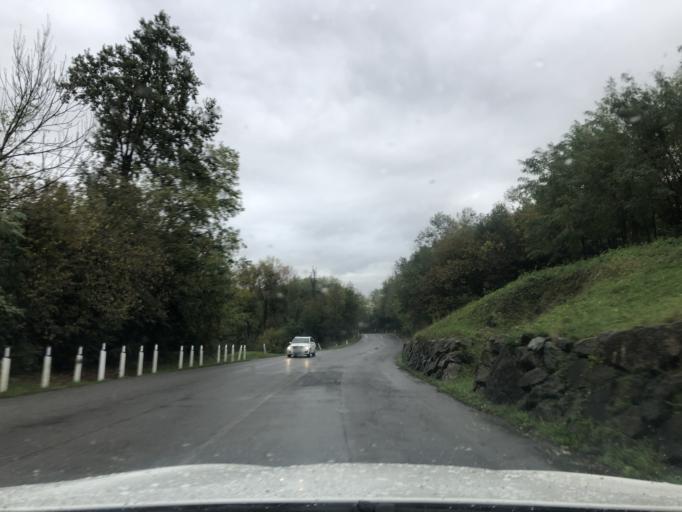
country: IT
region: Lombardy
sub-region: Provincia di Lecco
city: Suello
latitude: 45.8104
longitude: 9.3127
